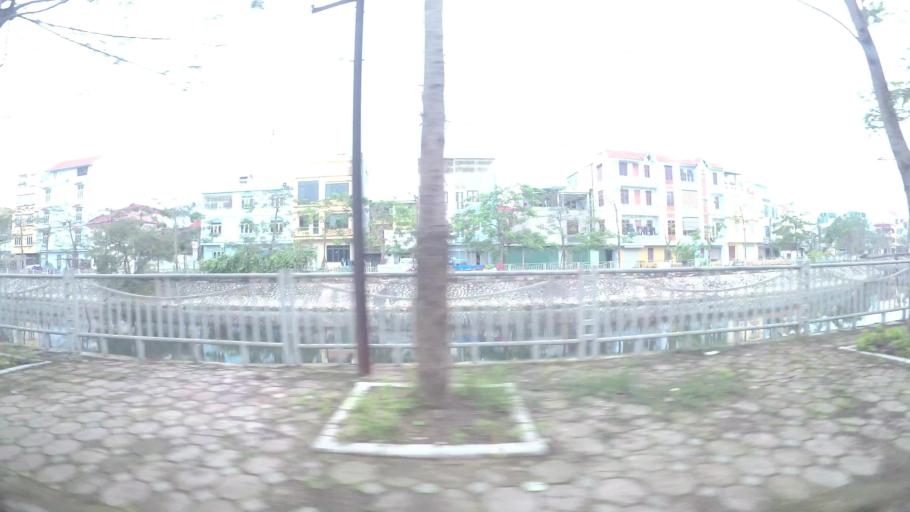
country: VN
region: Ha Noi
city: Van Dien
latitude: 20.9740
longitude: 105.8516
